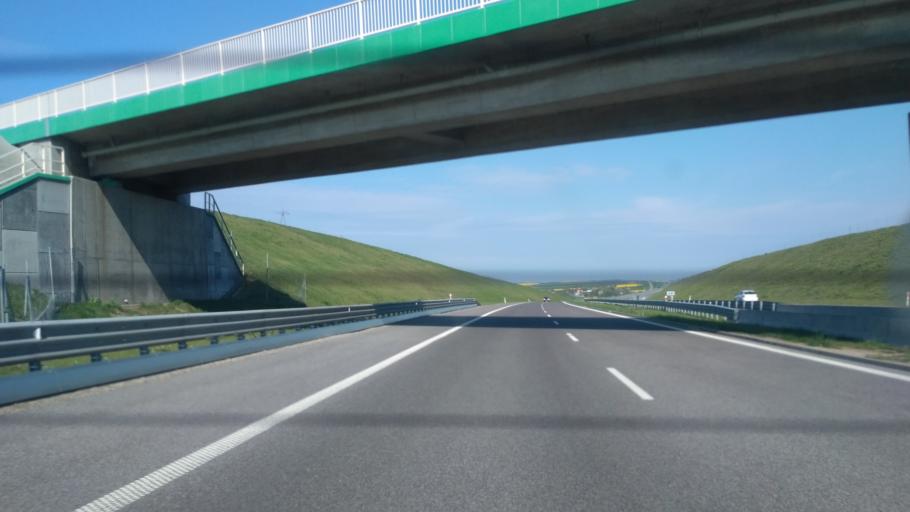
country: PL
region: Subcarpathian Voivodeship
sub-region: Powiat jaroslawski
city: Ostrow
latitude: 49.9195
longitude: 22.7410
